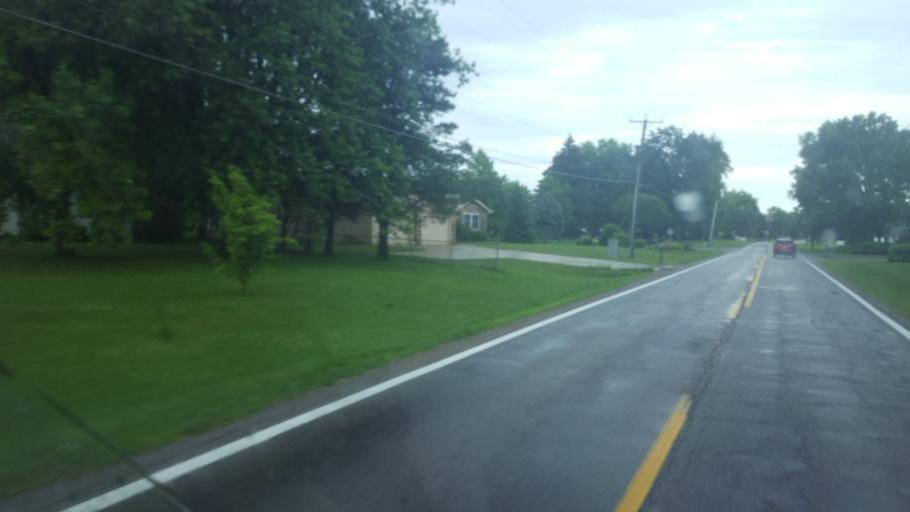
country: US
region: Ohio
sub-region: Marion County
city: Marion
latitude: 40.5622
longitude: -83.0839
